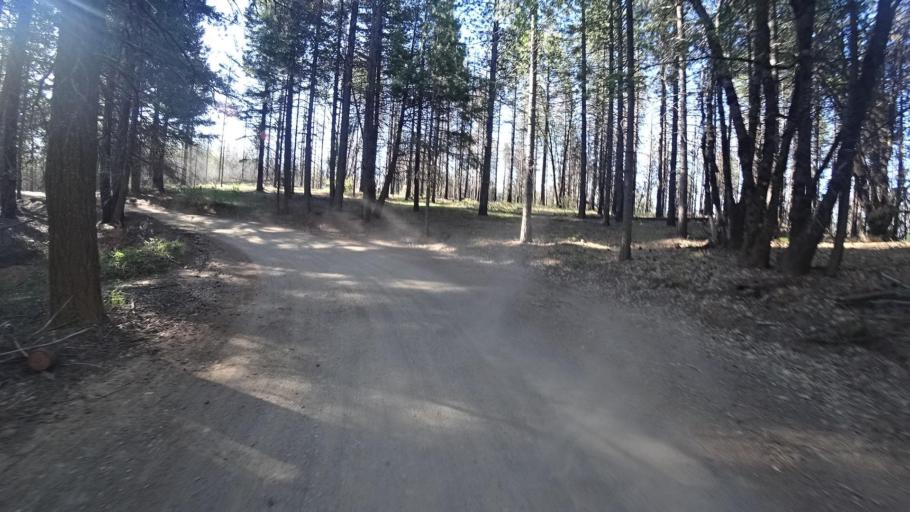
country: US
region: California
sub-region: Lake County
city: Upper Lake
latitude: 39.3515
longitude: -122.9766
